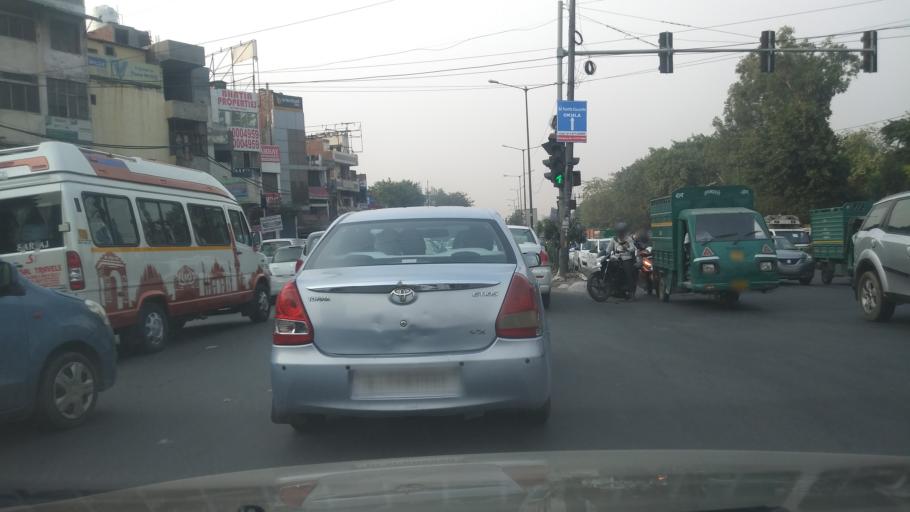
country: IN
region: Uttar Pradesh
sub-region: Gautam Buddha Nagar
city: Noida
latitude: 28.5367
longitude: 77.2675
